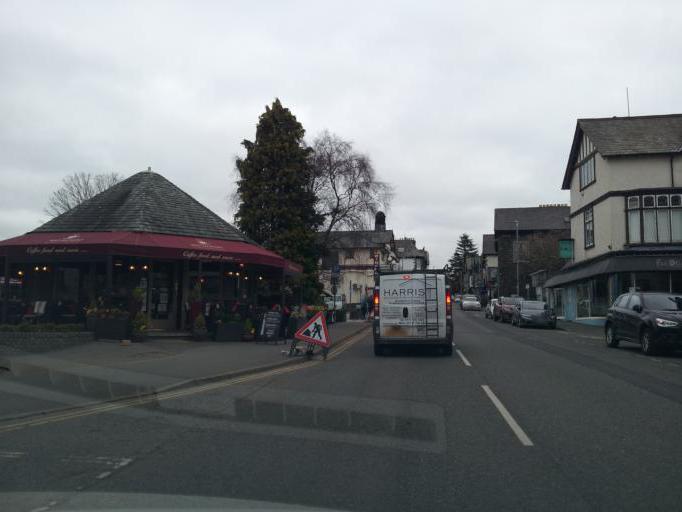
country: GB
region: England
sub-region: Cumbria
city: Windermere
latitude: 54.3660
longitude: -2.9177
